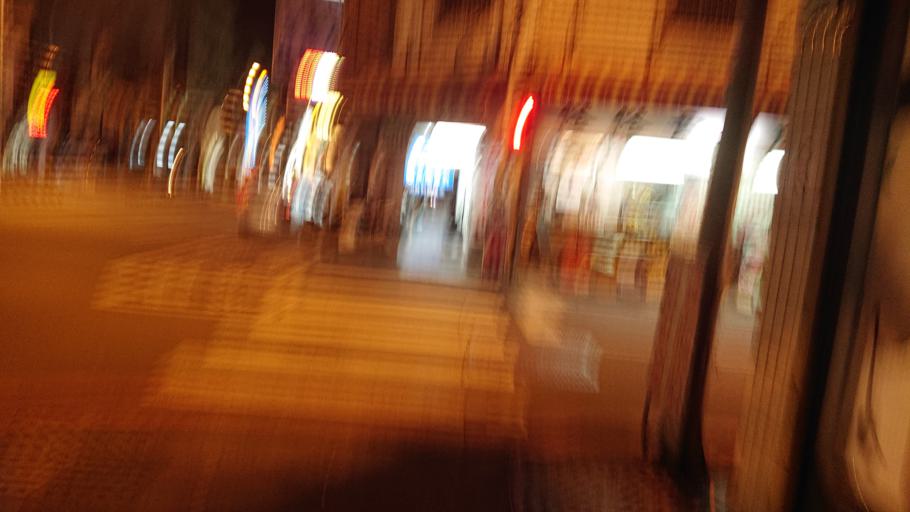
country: TW
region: Taiwan
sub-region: Tainan
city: Tainan
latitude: 22.9949
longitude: 120.1983
